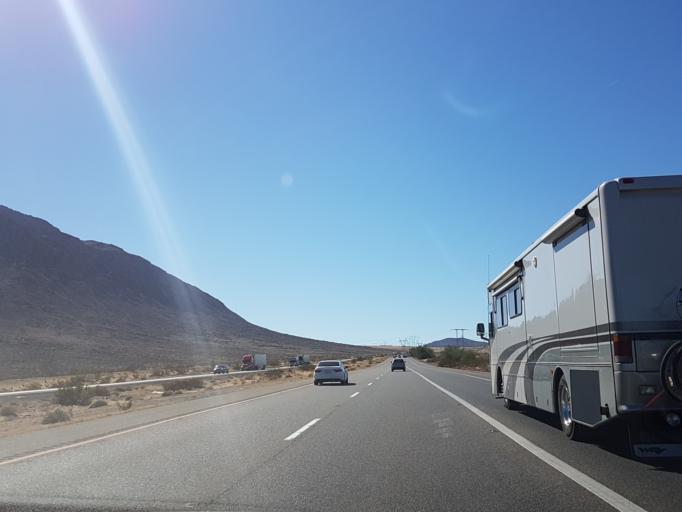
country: US
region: California
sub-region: San Bernardino County
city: Fort Irwin
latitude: 35.0934
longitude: -116.3063
